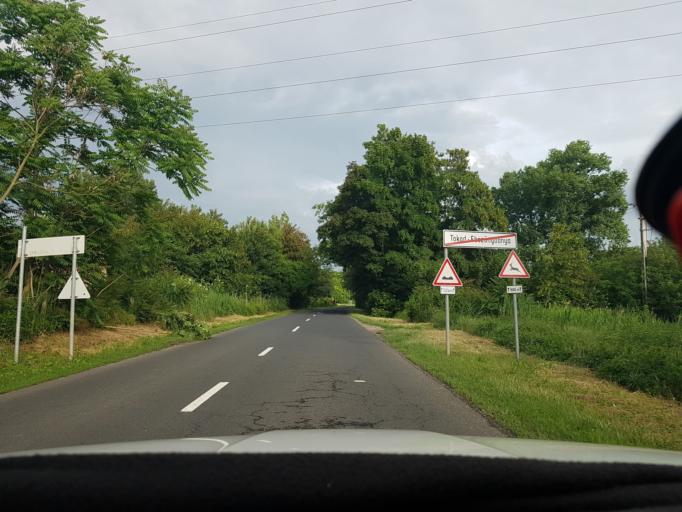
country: HU
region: Komarom-Esztergom
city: Tokod
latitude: 47.7024
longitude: 18.6518
